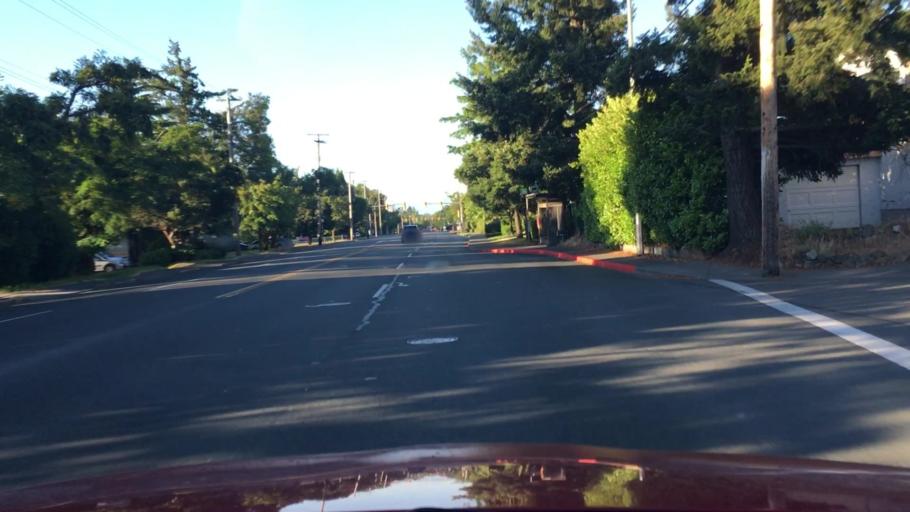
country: CA
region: British Columbia
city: Oak Bay
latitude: 48.4727
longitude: -123.3327
